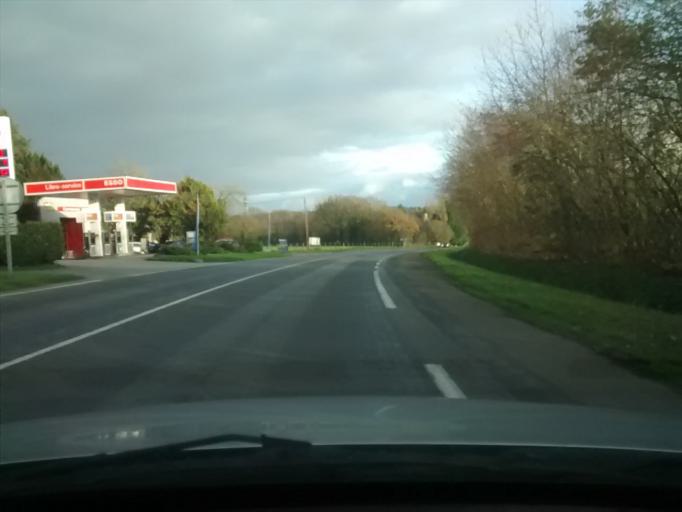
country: FR
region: Pays de la Loire
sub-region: Departement de la Mayenne
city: Saint-Pierre-la-Cour
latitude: 48.0741
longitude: -1.0163
